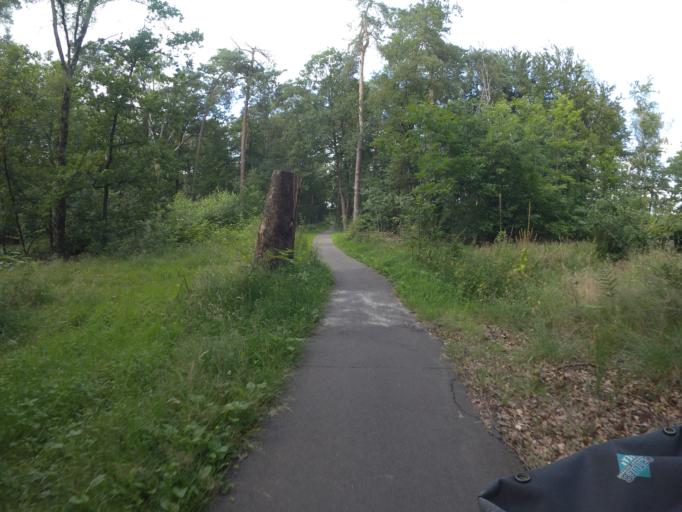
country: NL
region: North Brabant
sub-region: Gemeente Heeze-Leende
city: Heeze
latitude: 51.3895
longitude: 5.5268
